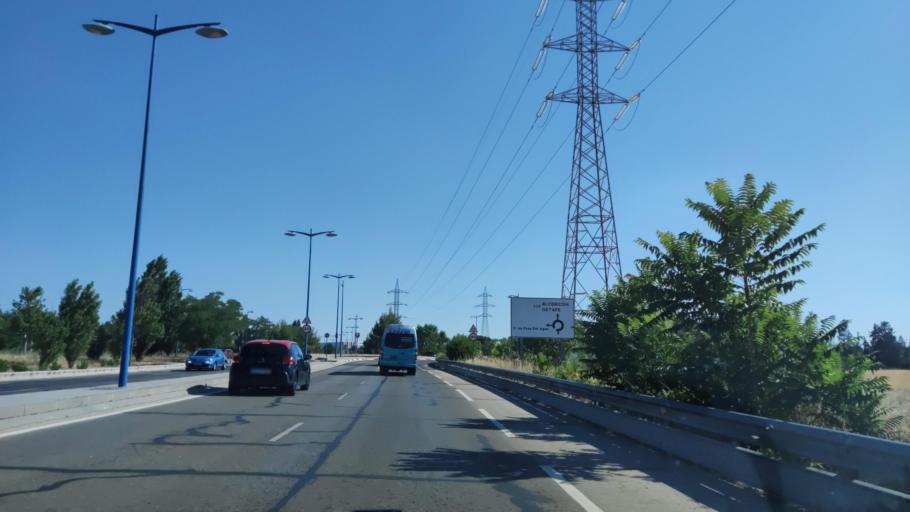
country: ES
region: Madrid
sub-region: Provincia de Madrid
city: Leganes
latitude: 40.3416
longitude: -3.7876
